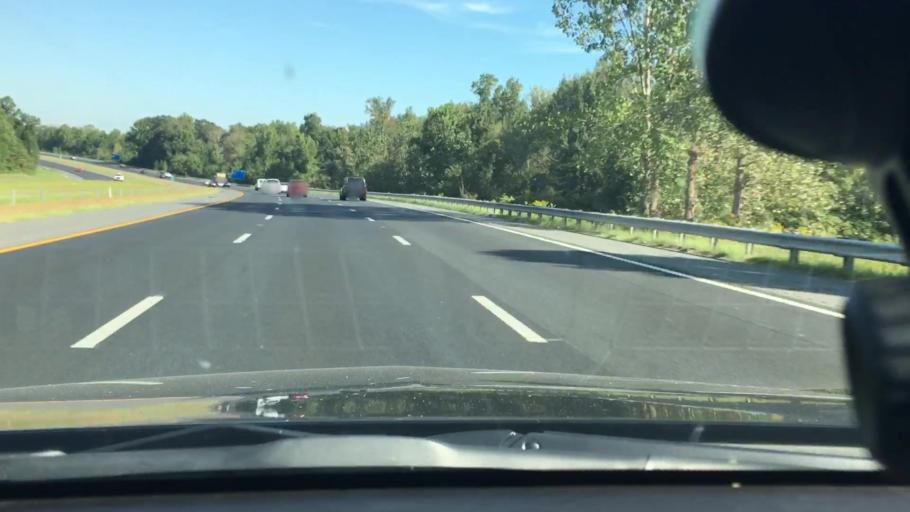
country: US
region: North Carolina
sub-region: Mecklenburg County
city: Mint Hill
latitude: 35.2428
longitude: -80.6495
